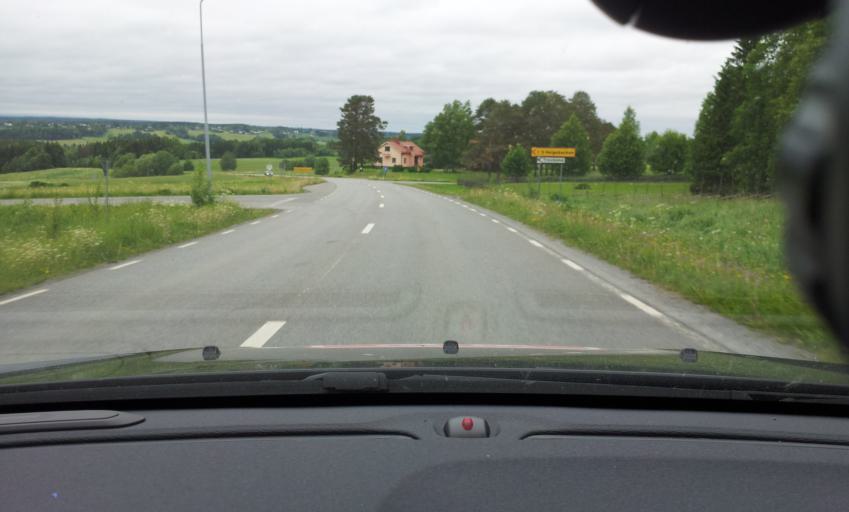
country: SE
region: Jaemtland
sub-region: Bergs Kommun
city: Hoverberg
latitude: 62.9988
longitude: 14.3897
